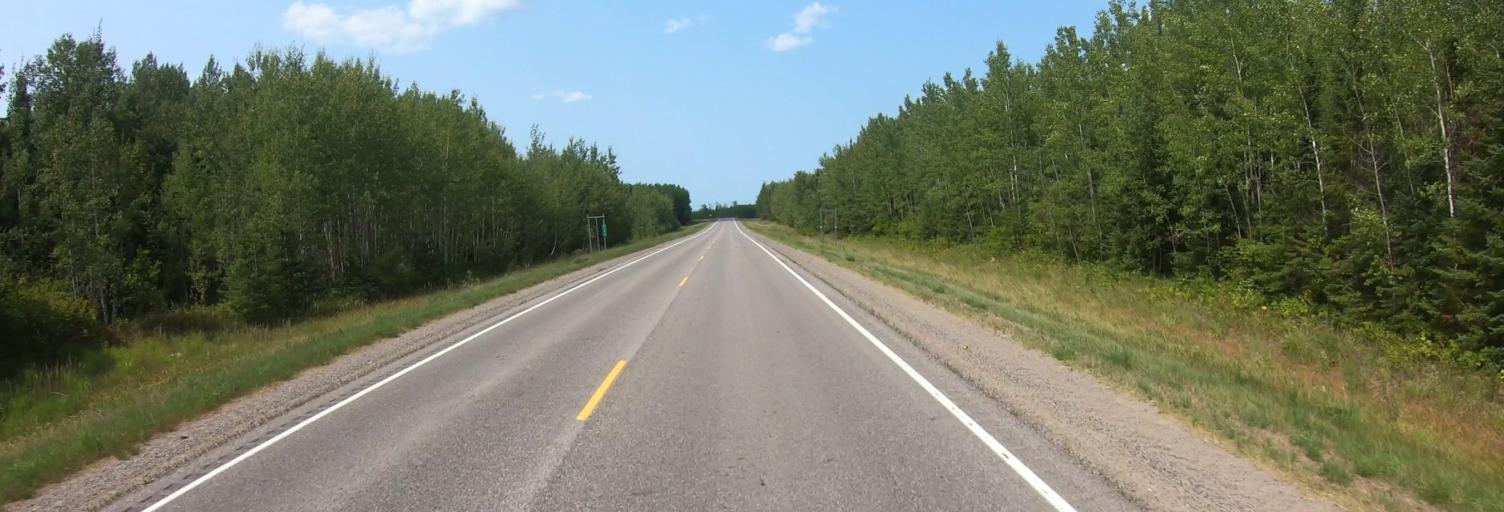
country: US
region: Minnesota
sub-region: Lake of the Woods County
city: Baudette
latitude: 48.6387
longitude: -94.1302
